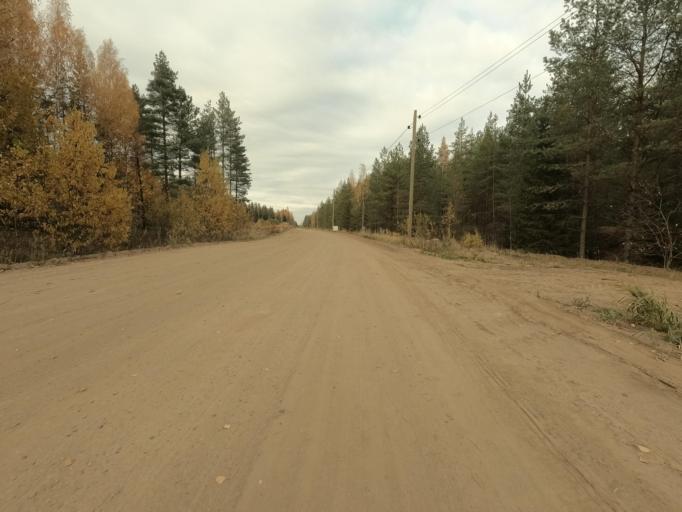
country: RU
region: Leningrad
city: Priladozhskiy
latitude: 59.6893
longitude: 31.3606
